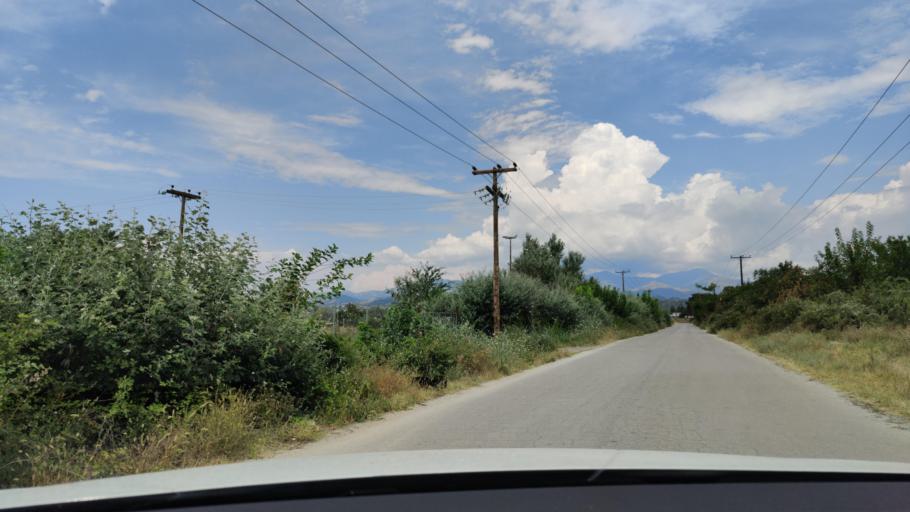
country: GR
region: Central Macedonia
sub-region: Nomos Serron
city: Serres
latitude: 41.0685
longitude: 23.5561
